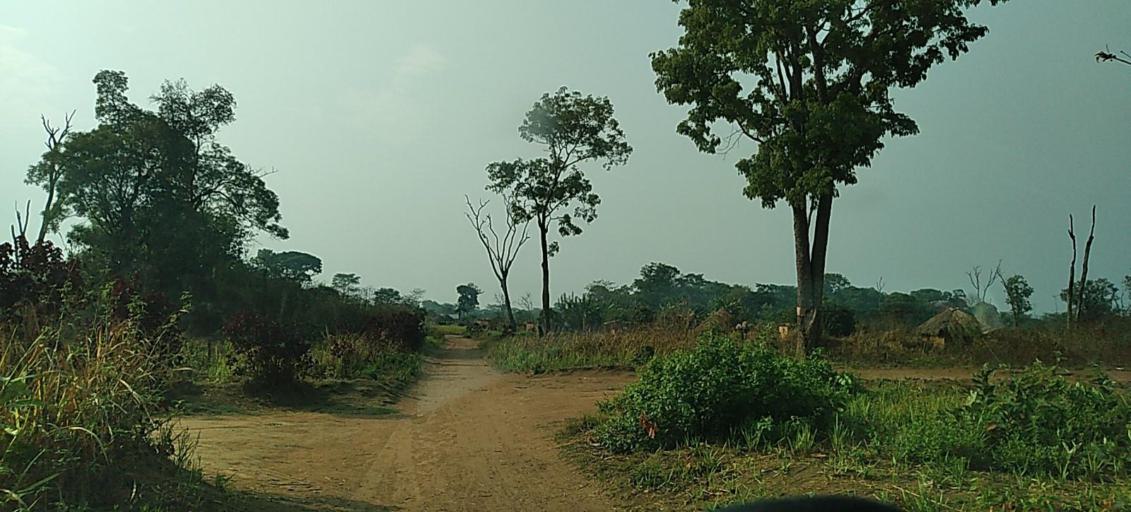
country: ZM
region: North-Western
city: Solwezi
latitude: -12.3651
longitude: 26.5551
